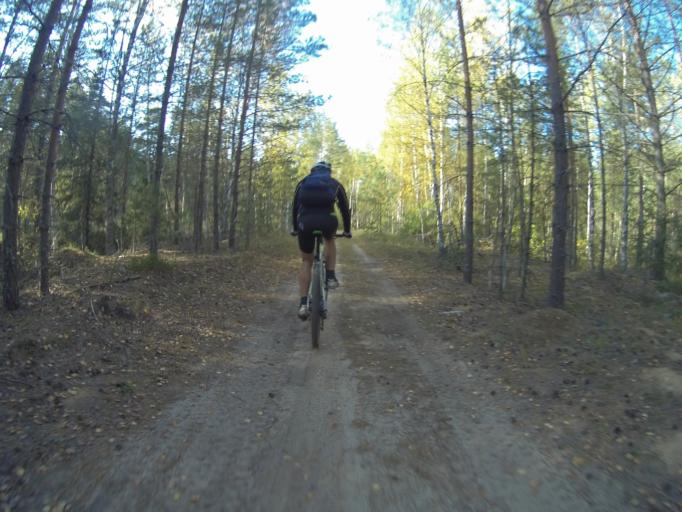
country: RU
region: Vladimir
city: Sobinka
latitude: 55.9220
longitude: 40.0678
